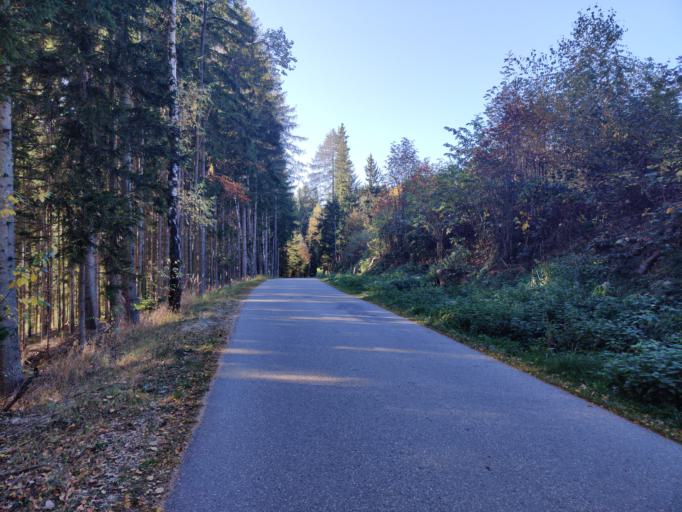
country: AT
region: Styria
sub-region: Politischer Bezirk Hartberg-Fuerstenfeld
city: Sankt Jakob im Walde
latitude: 47.4676
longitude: 15.8054
